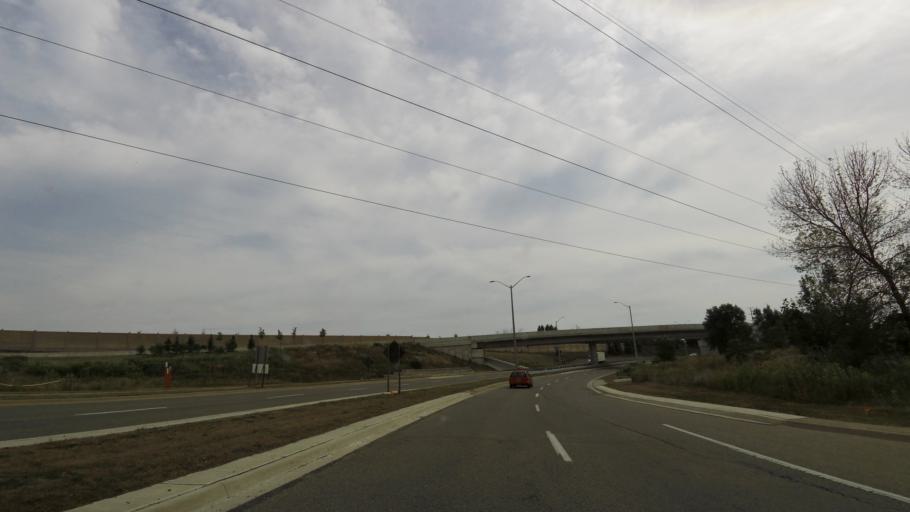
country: CA
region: Ontario
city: Etobicoke
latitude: 43.6363
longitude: -79.6081
